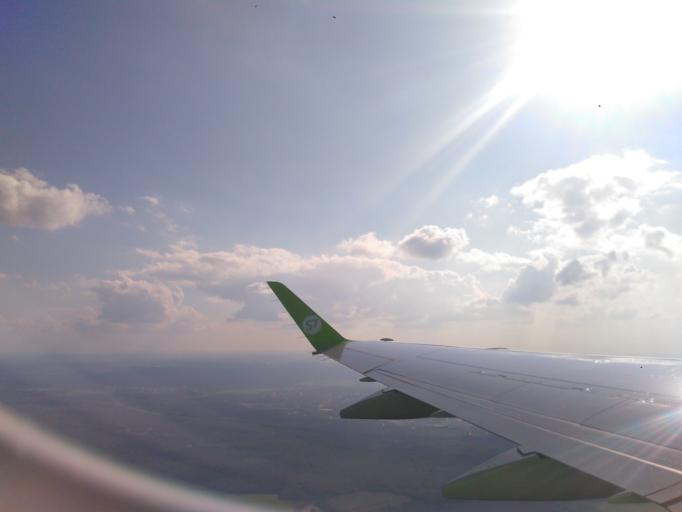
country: RU
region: Moskovskaya
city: Vostryakovo
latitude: 55.4631
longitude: 37.8592
